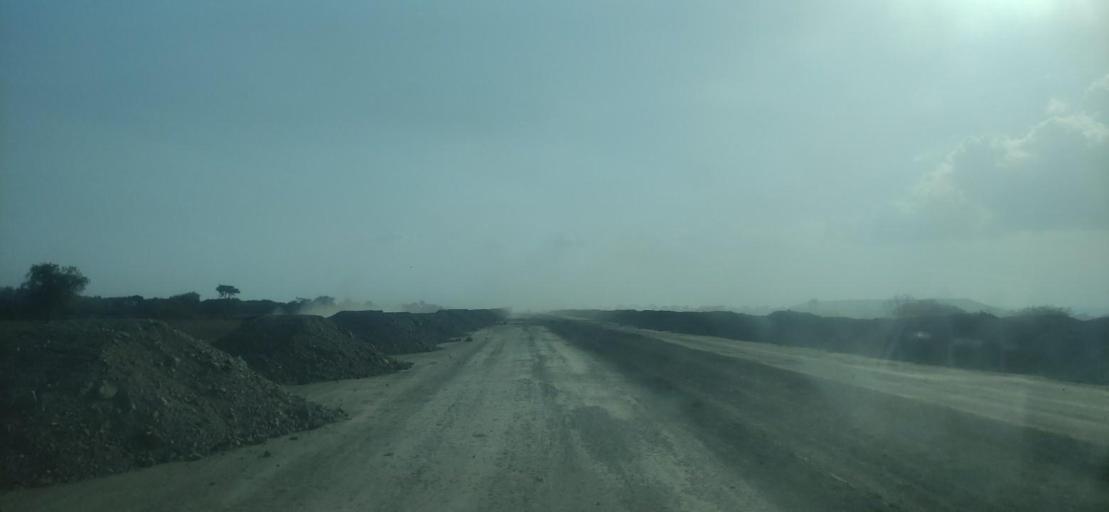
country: ET
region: Southern Nations, Nationalities, and People's Region
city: Hawassa
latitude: 7.1702
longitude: 38.4887
